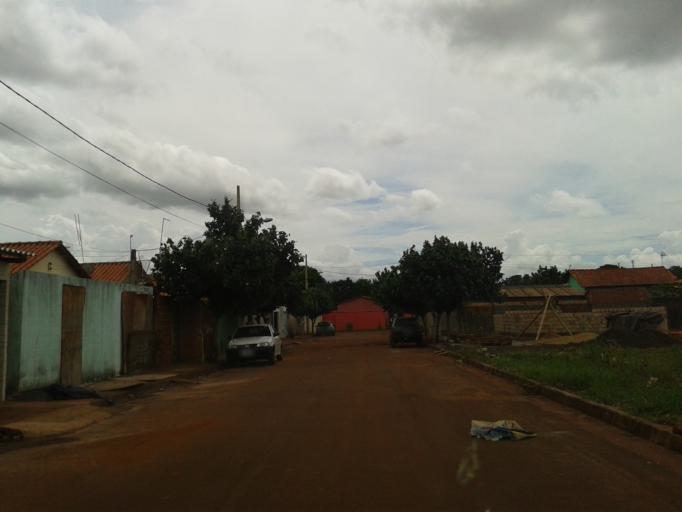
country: BR
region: Minas Gerais
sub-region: Centralina
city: Centralina
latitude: -18.5849
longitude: -49.2061
